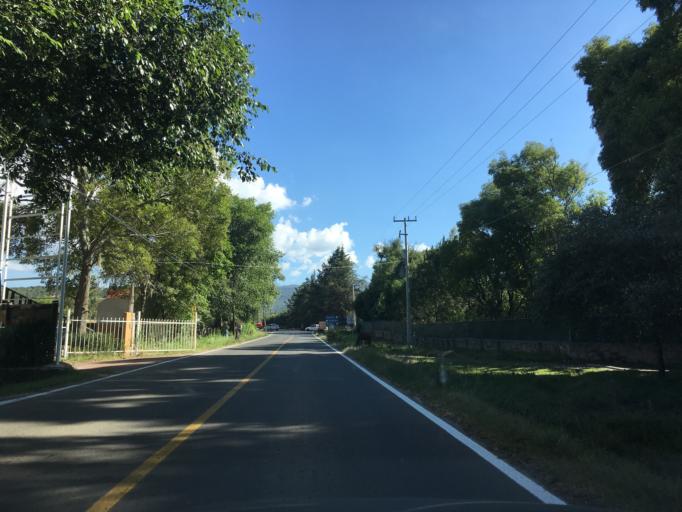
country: MX
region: Hidalgo
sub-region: Omitlan de Juarez
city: San Antonio el Paso
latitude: 20.2152
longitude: -98.5658
